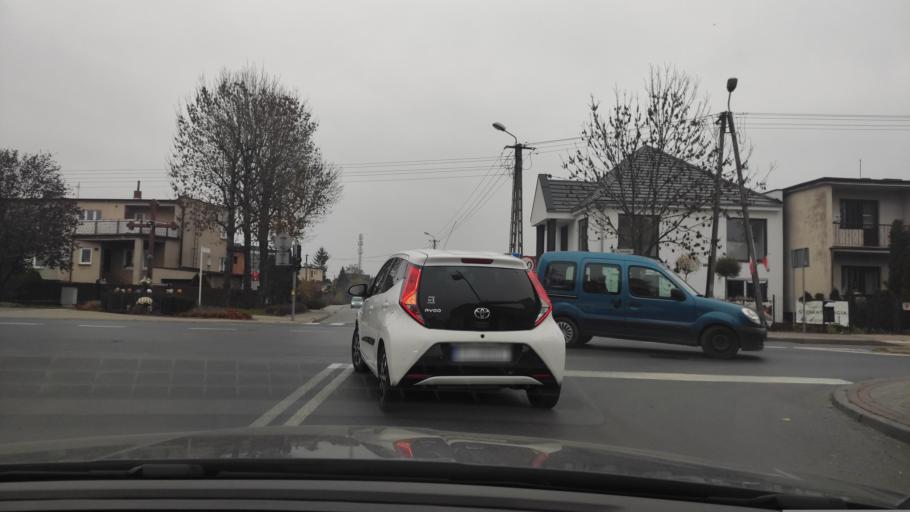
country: PL
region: Greater Poland Voivodeship
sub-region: Powiat poznanski
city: Kostrzyn
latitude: 52.3974
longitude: 17.2186
